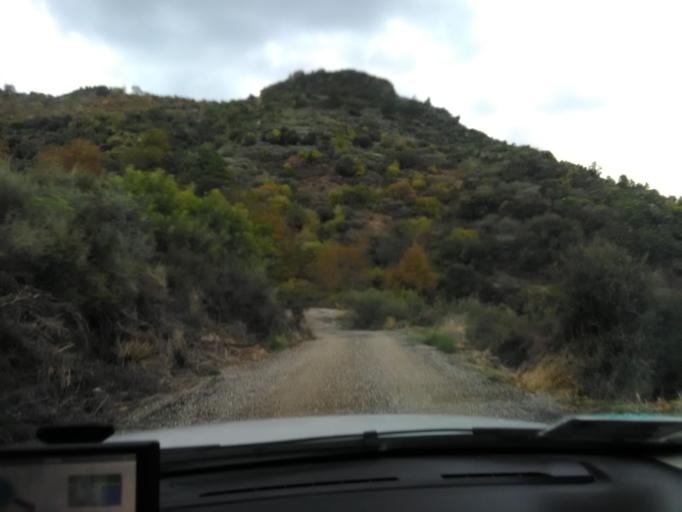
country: TR
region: Antalya
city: Gazipasa
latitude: 36.1579
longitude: 32.4198
